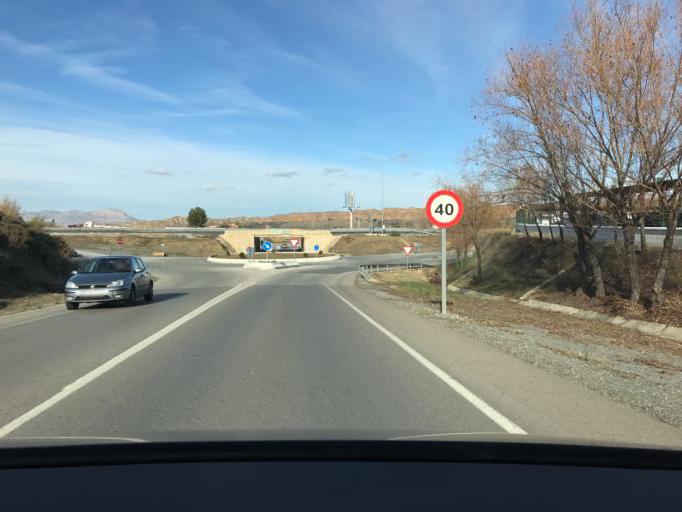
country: ES
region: Andalusia
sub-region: Provincia de Granada
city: Guadix
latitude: 37.3196
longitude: -3.1598
